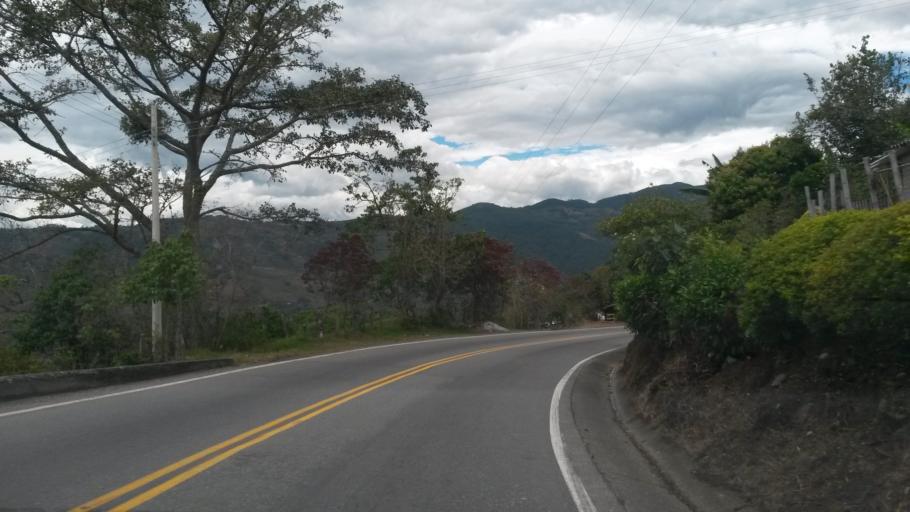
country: CO
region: Cauca
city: Rosas
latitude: 2.2747
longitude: -76.7230
